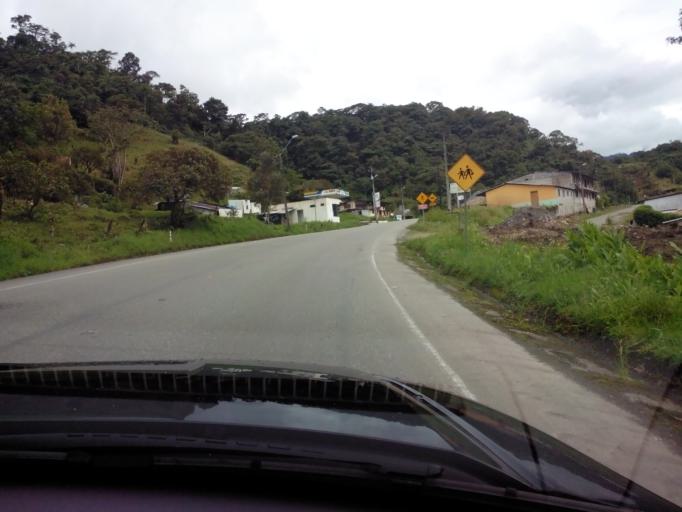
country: EC
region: Napo
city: Archidona
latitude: -0.5807
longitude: -77.8667
